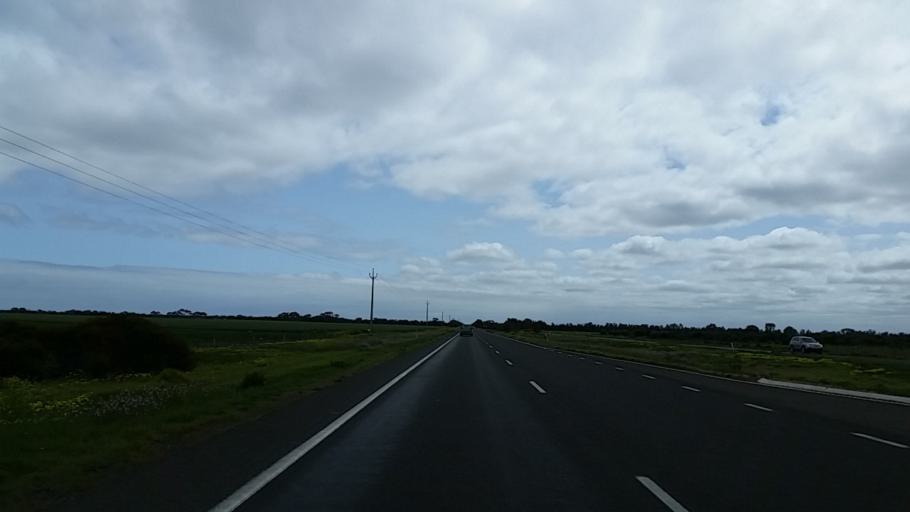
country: AU
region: South Australia
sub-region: Mallala
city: Two Wells
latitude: -34.5690
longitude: 138.4795
